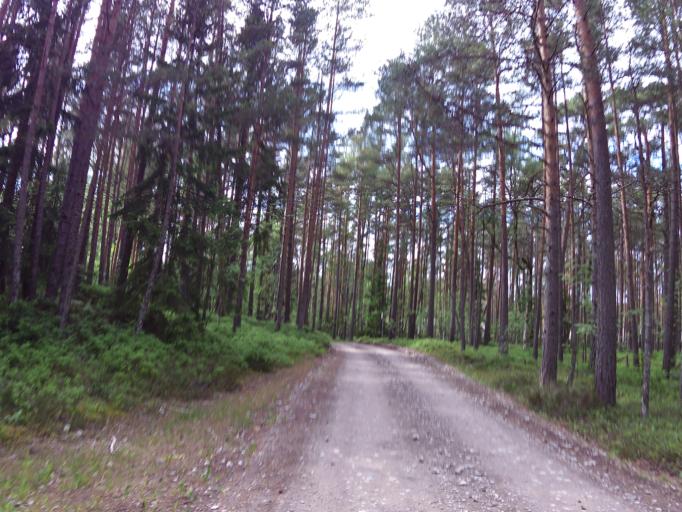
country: EE
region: Laeaene
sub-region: Ridala Parish
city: Uuemoisa
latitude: 59.2236
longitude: 23.6972
